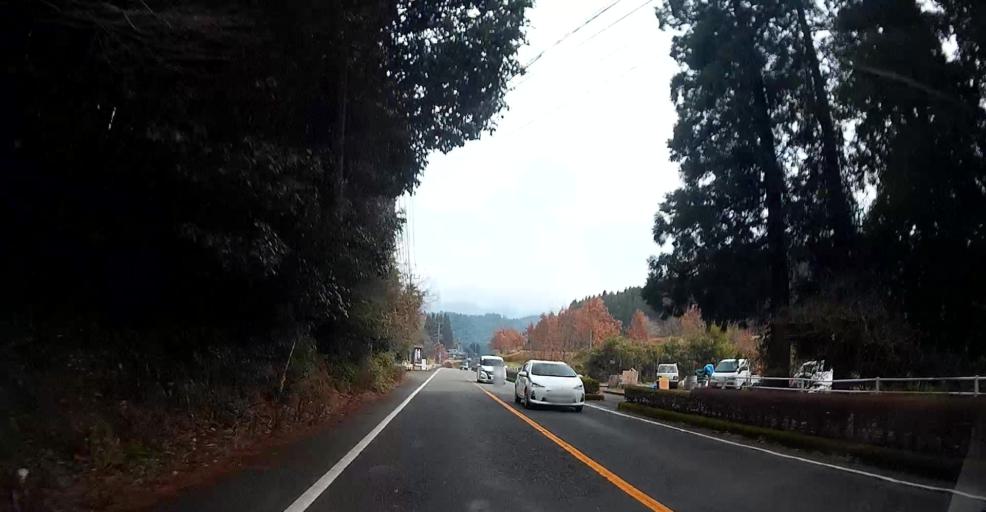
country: JP
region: Kumamoto
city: Matsubase
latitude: 32.6258
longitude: 130.8847
